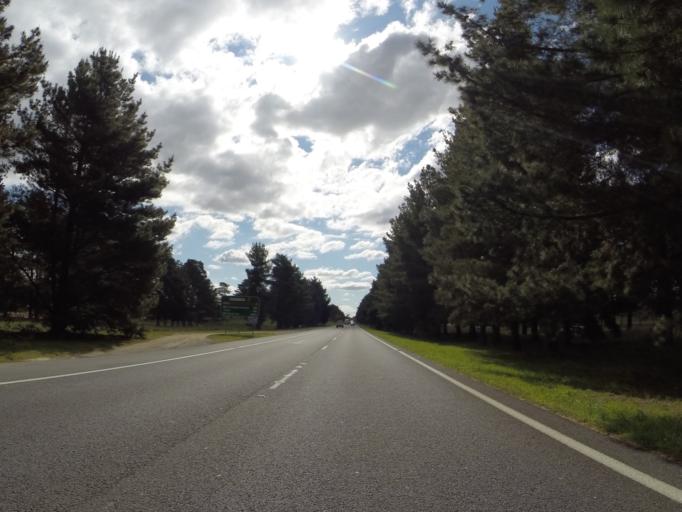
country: AU
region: Australian Capital Territory
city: Belconnen
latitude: -35.1992
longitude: 149.0917
